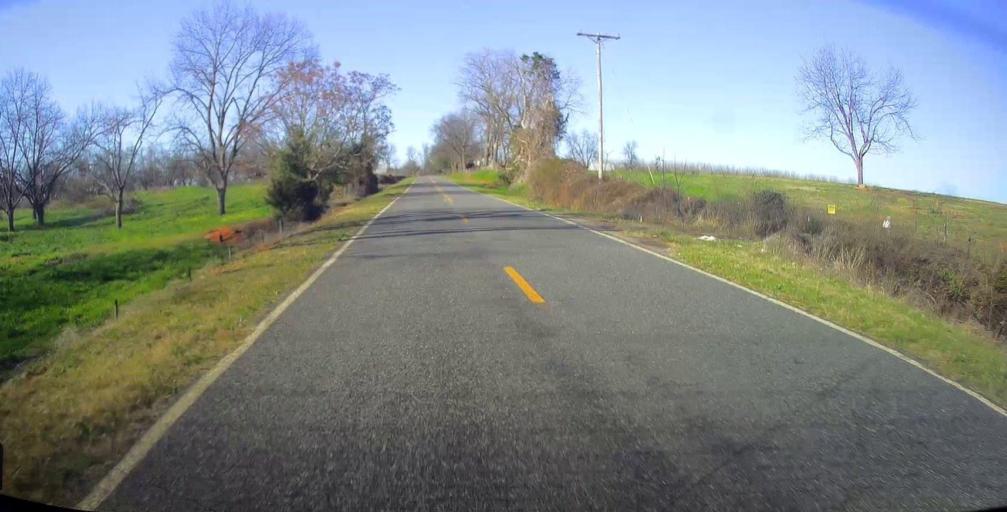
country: US
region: Georgia
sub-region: Peach County
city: Fort Valley
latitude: 32.6135
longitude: -83.8521
